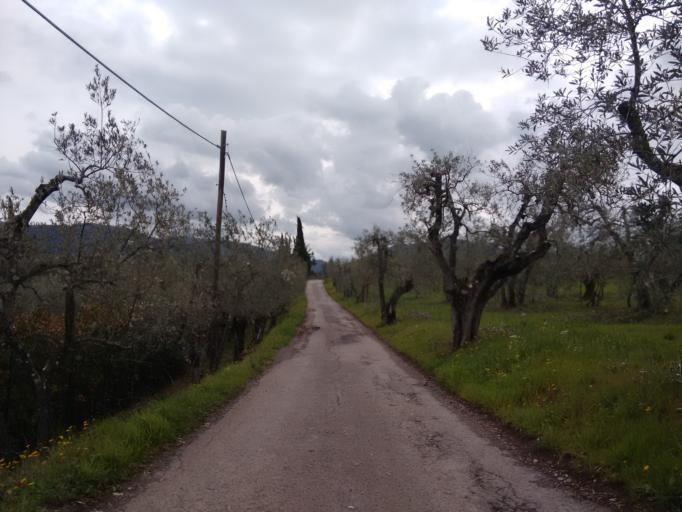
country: IT
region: Tuscany
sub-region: Province of Florence
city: Strada in Chianti
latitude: 43.6608
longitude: 11.3070
